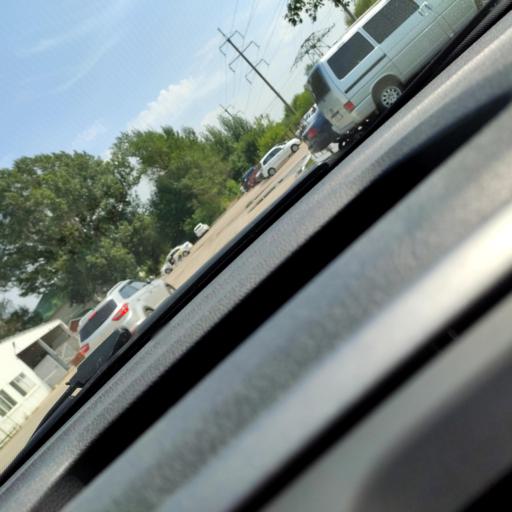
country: RU
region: Samara
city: Tol'yatti
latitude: 53.5836
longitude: 49.2504
